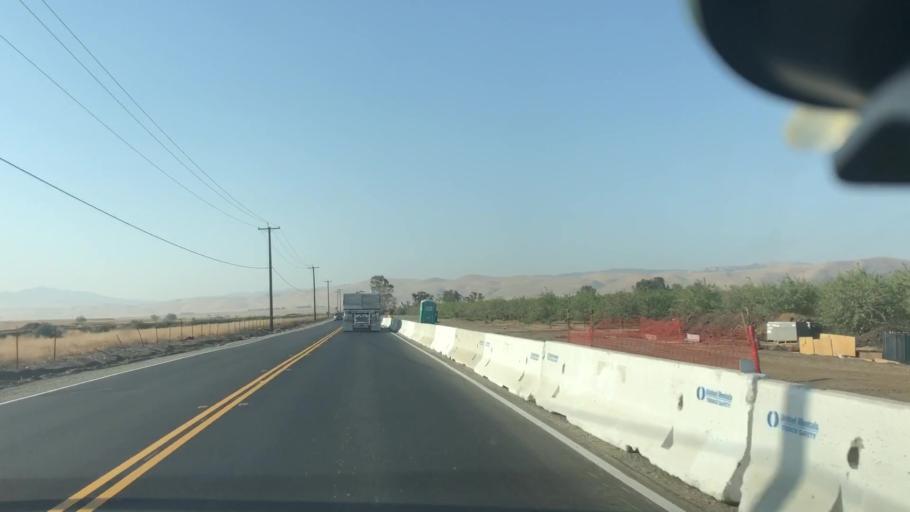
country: US
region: California
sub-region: San Joaquin County
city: Tracy
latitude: 37.6846
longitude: -121.4528
